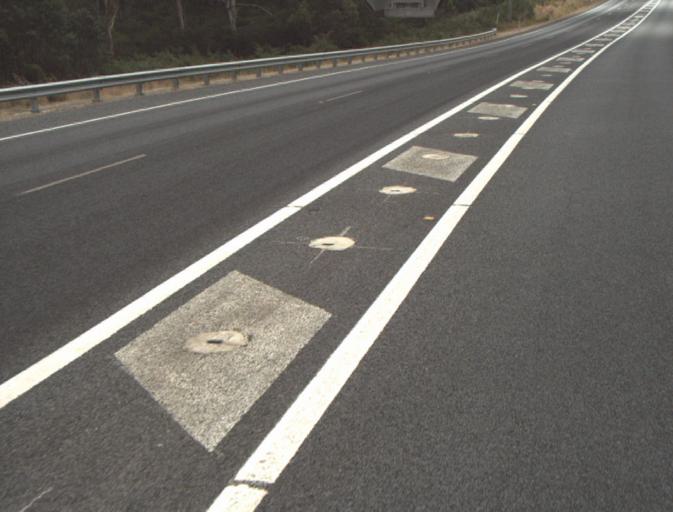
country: AU
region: Tasmania
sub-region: Launceston
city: Mayfield
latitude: -41.2898
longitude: 147.0434
